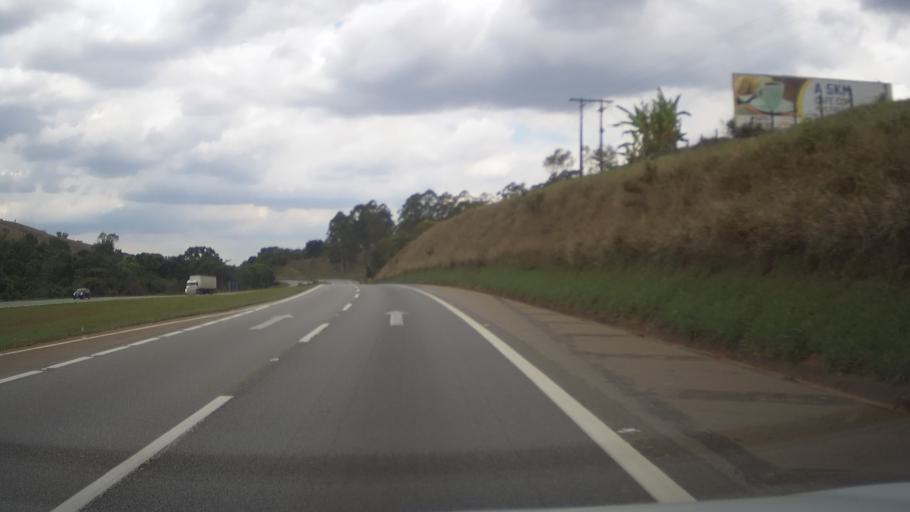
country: BR
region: Minas Gerais
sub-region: Tres Coracoes
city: Tres Coracoes
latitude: -21.5254
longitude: -45.2263
